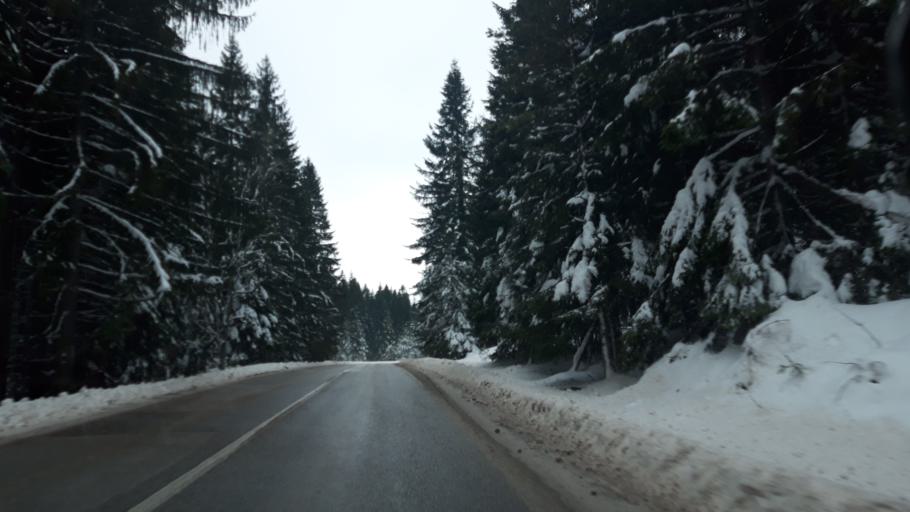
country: BA
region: Republika Srpska
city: Han Pijesak
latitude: 44.0541
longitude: 18.9357
